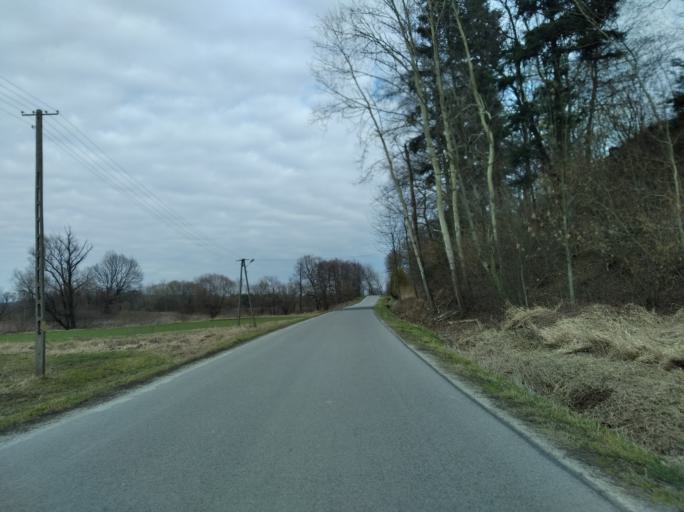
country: PL
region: Subcarpathian Voivodeship
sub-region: Powiat strzyzowski
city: Frysztak
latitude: 49.8564
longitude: 21.6288
